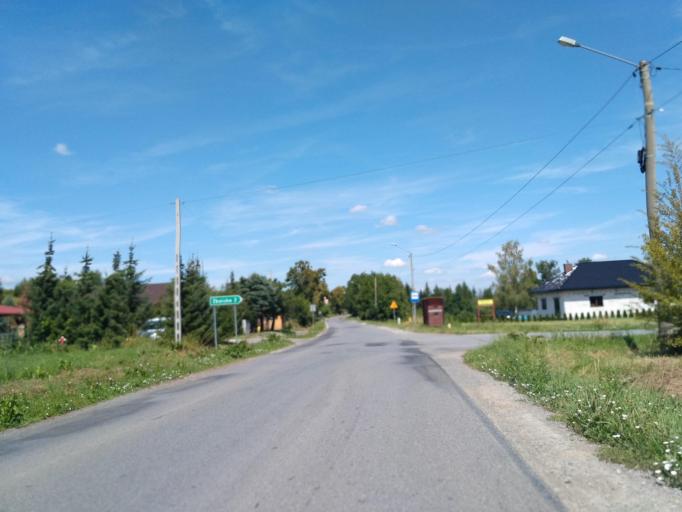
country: PL
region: Subcarpathian Voivodeship
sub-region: Powiat sanocki
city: Bukowsko
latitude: 49.5204
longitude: 22.1013
